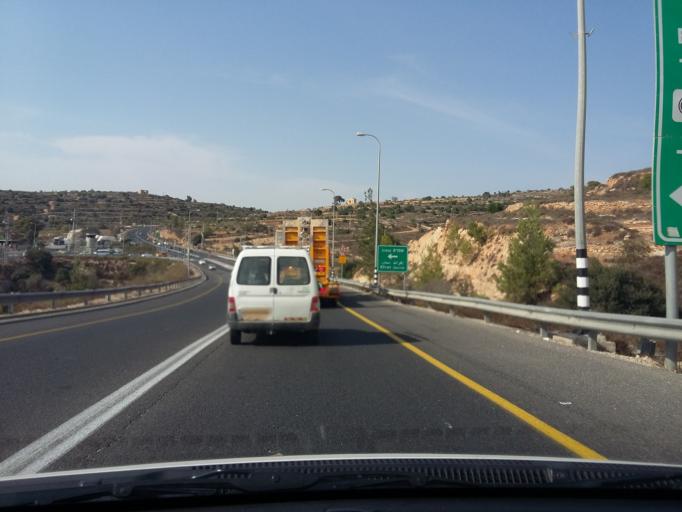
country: PS
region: West Bank
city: Al Khadir
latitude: 31.6880
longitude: 35.1612
